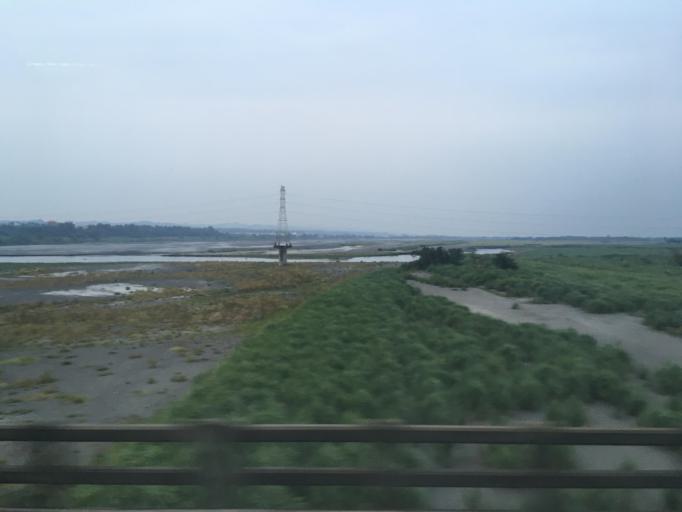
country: TW
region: Taiwan
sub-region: Pingtung
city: Pingtung
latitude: 22.6623
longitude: 120.4348
